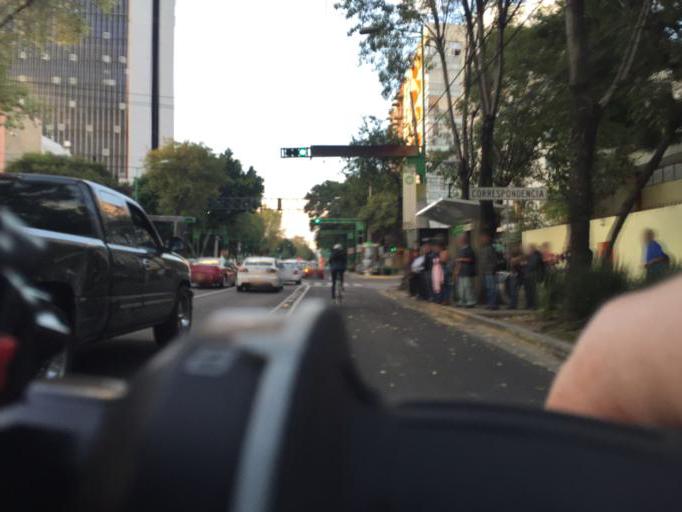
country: MX
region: Mexico City
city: Benito Juarez
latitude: 19.3922
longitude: -99.1464
